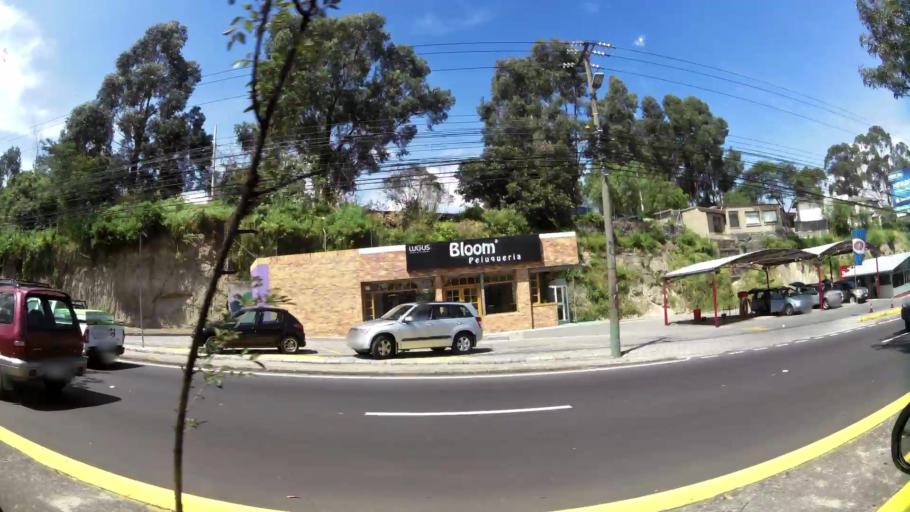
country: EC
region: Pichincha
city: Quito
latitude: -0.2104
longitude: -78.4180
